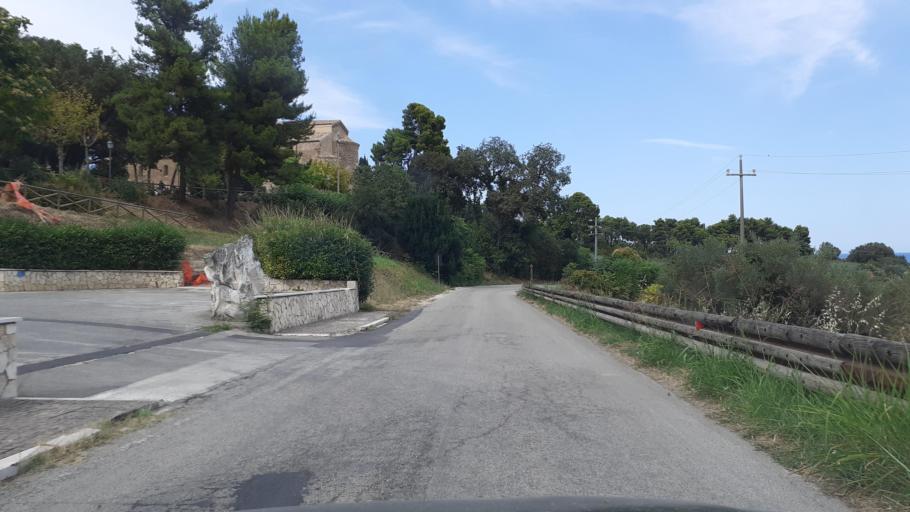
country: IT
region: Abruzzo
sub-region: Provincia di Chieti
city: Fossacesia
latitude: 42.2534
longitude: 14.4988
